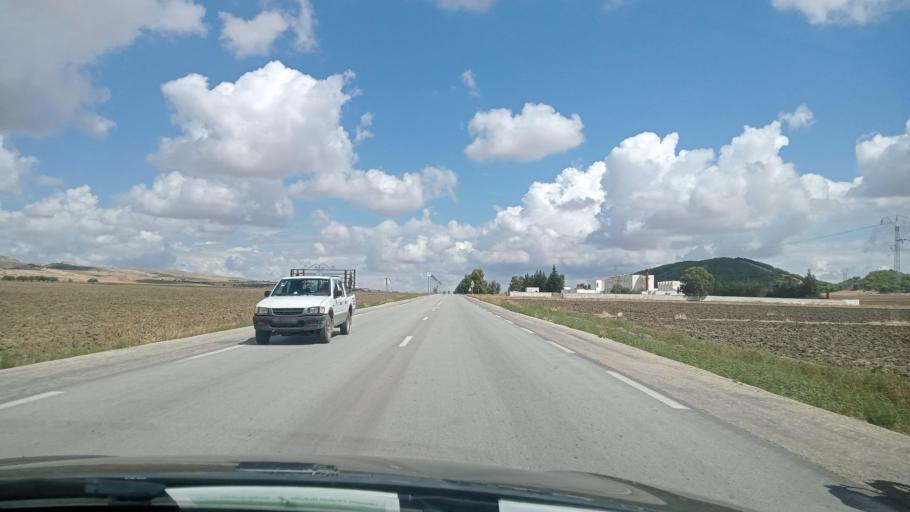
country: TN
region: Silyanah
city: Al Karib
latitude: 36.3147
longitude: 9.1103
